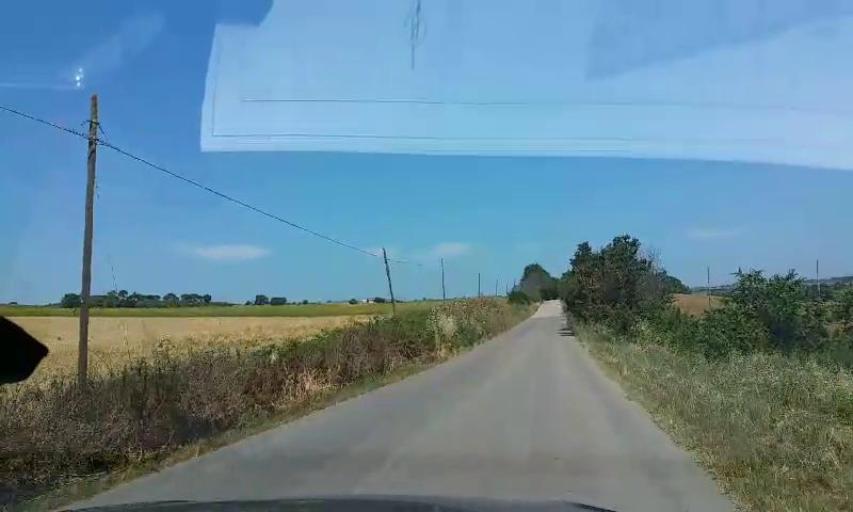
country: IT
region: Molise
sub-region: Provincia di Campobasso
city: Guglionesi
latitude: 41.9571
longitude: 14.9004
